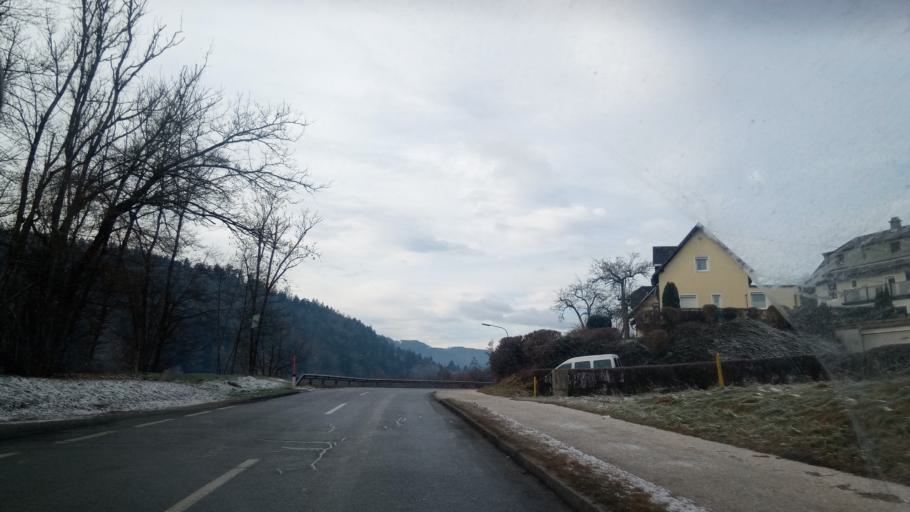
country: AT
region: Carinthia
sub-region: Politischer Bezirk Klagenfurt Land
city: Kottmannsdorf
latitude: 46.5902
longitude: 14.2591
